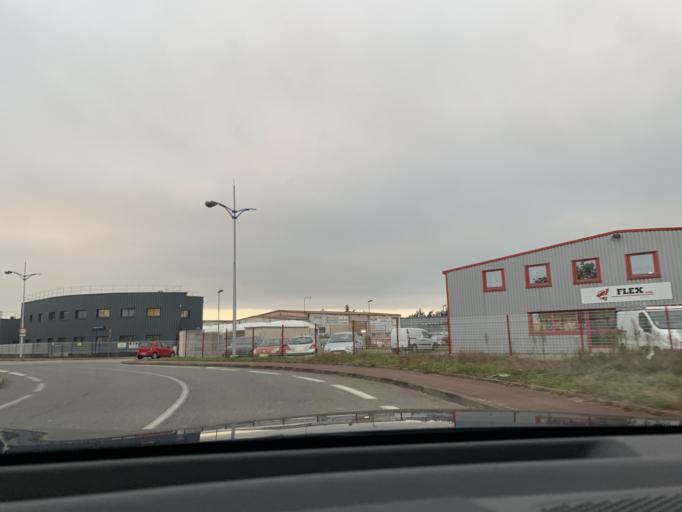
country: FR
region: Rhone-Alpes
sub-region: Departement du Rhone
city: Corbas
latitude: 45.6700
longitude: 4.9123
